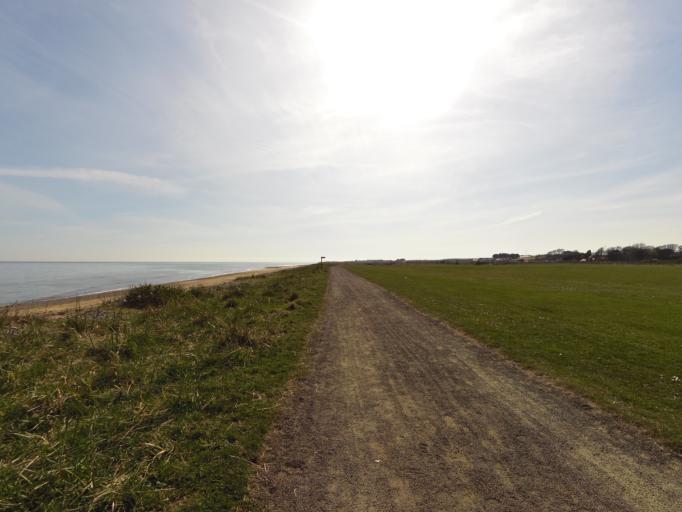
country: GB
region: Scotland
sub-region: Angus
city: Arbroath
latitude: 56.5461
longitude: -2.6146
